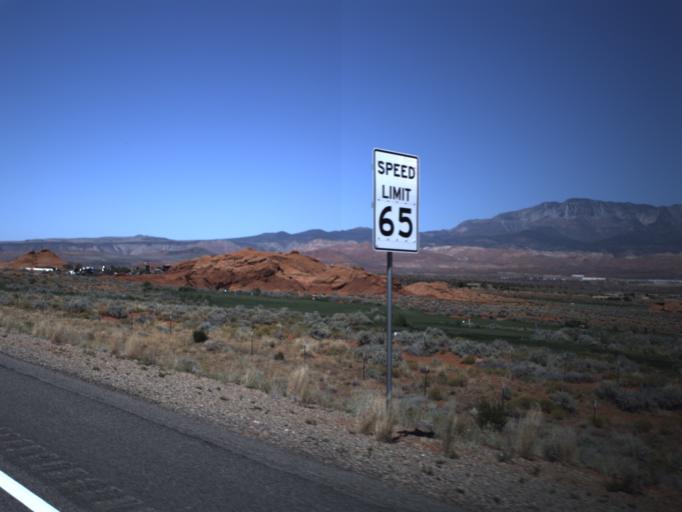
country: US
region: Utah
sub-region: Washington County
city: Washington
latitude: 37.1098
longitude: -113.4088
